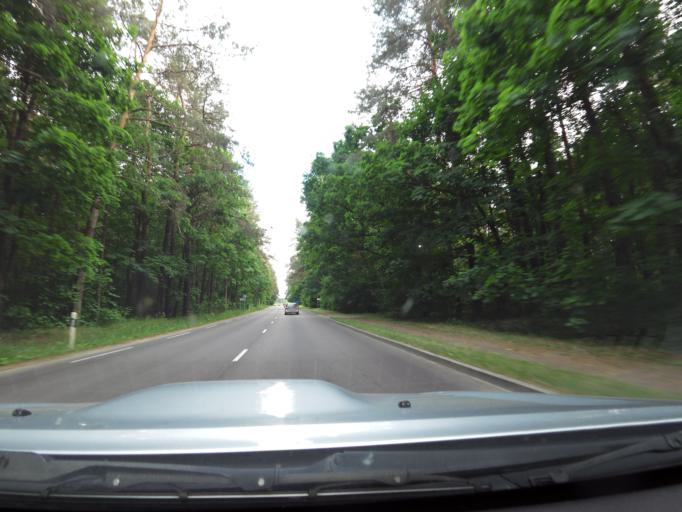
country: LT
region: Vilnius County
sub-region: Vilniaus Rajonas
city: Vievis
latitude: 54.7657
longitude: 24.8385
